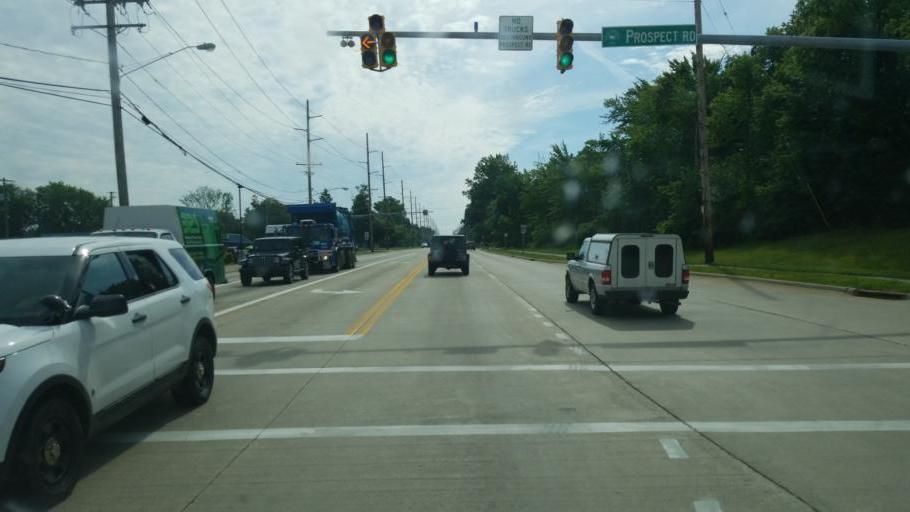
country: US
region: Ohio
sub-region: Cuyahoga County
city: Strongsville
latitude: 41.3124
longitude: -81.8578
